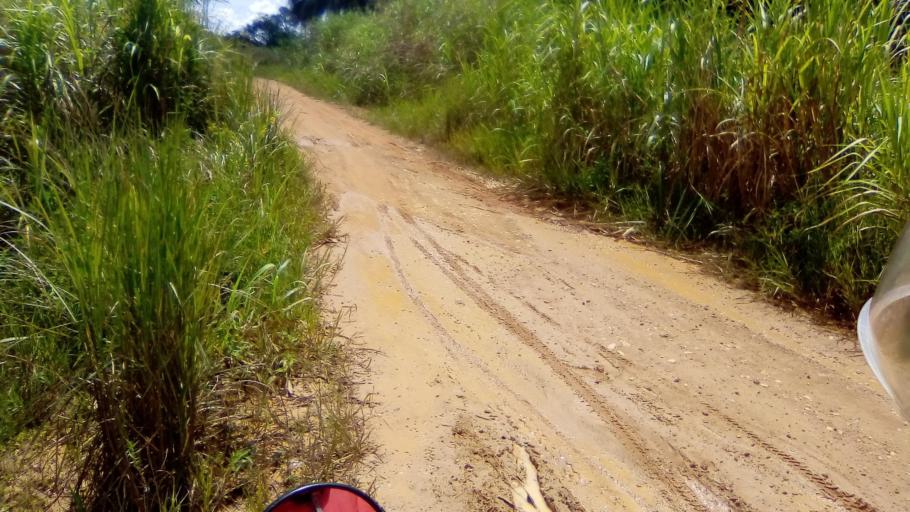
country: SL
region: Eastern Province
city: Simbakoro
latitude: 8.5448
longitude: -10.9349
